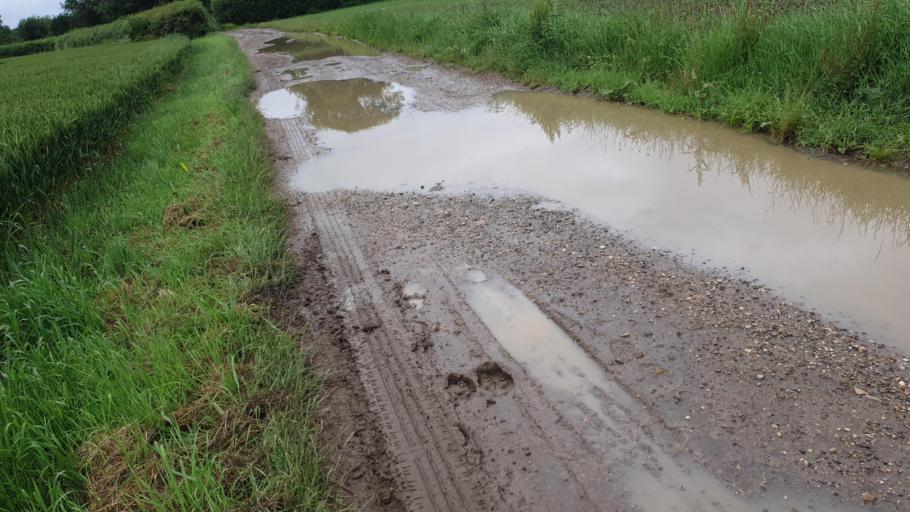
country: GB
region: England
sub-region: Essex
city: Great Bentley
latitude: 51.8810
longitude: 1.0593
